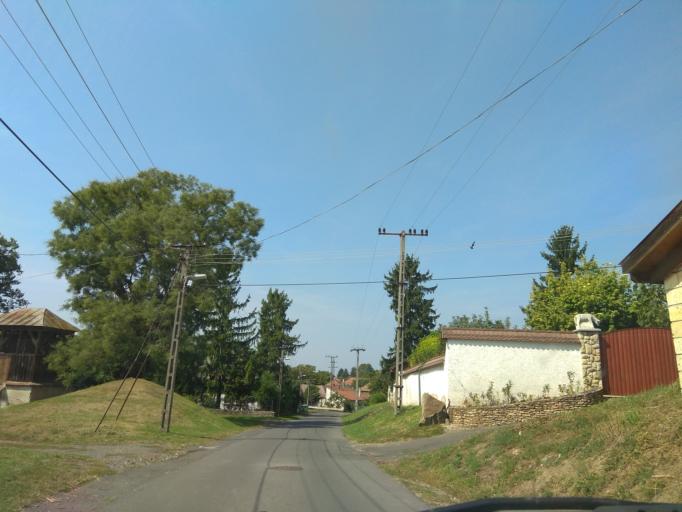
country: HU
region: Borsod-Abauj-Zemplen
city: Tallya
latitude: 48.2332
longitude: 21.2314
